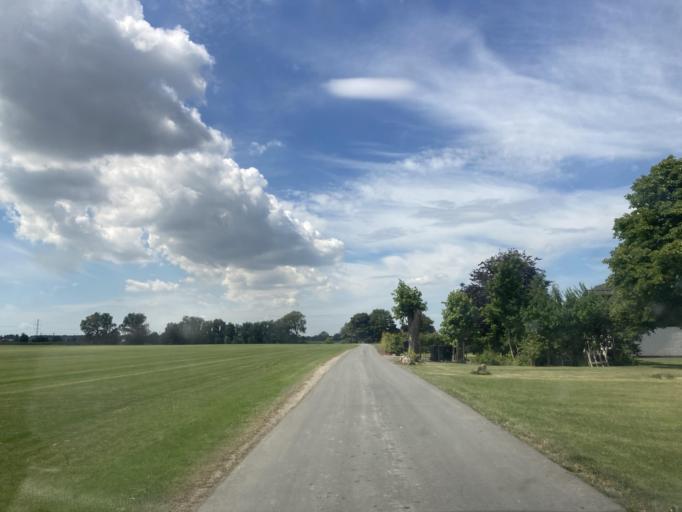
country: DK
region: Zealand
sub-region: Koge Kommune
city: Borup
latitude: 55.4601
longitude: 11.9735
